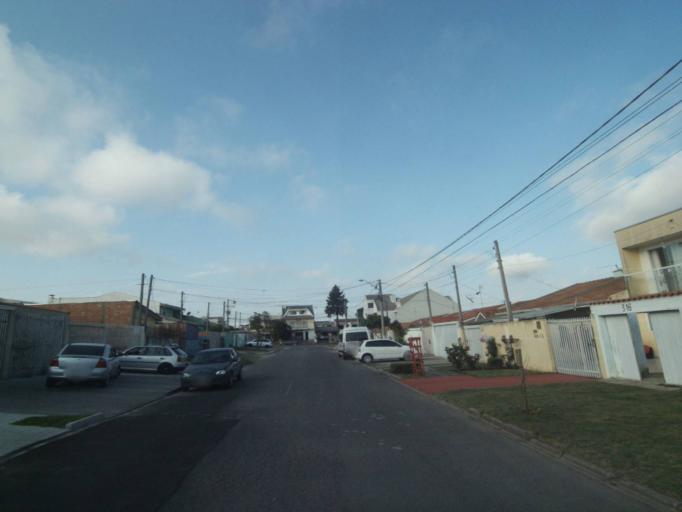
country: BR
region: Parana
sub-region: Sao Jose Dos Pinhais
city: Sao Jose dos Pinhais
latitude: -25.5483
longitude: -49.2547
